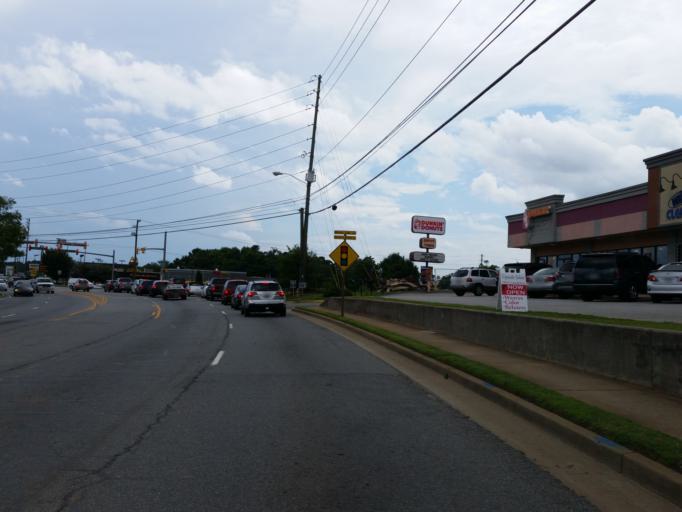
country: US
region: Georgia
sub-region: Cobb County
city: Kennesaw
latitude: 34.0618
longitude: -84.5928
